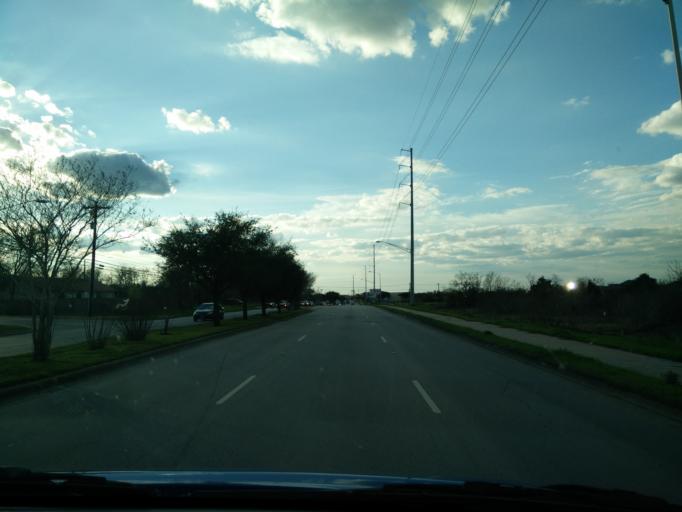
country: US
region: Texas
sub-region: Travis County
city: Austin
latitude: 30.2229
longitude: -97.6984
